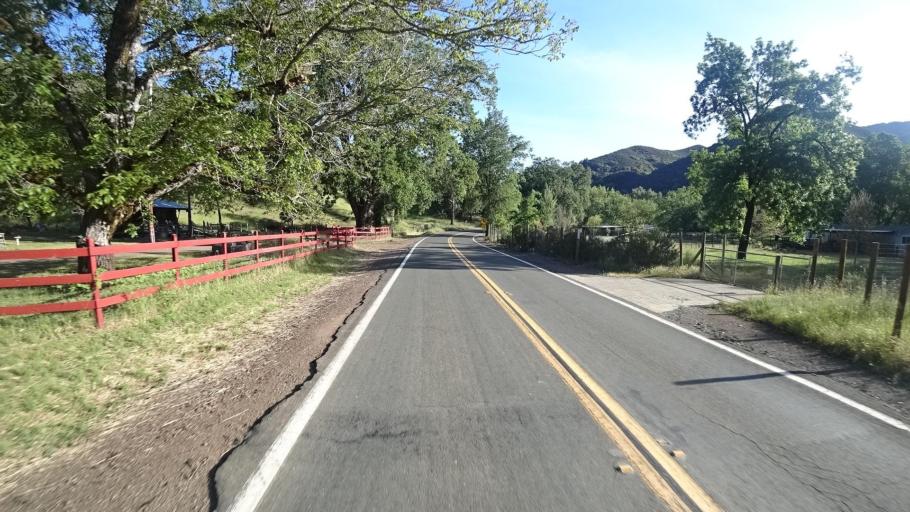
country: US
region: California
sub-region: Lake County
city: Upper Lake
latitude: 39.1346
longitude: -122.9983
